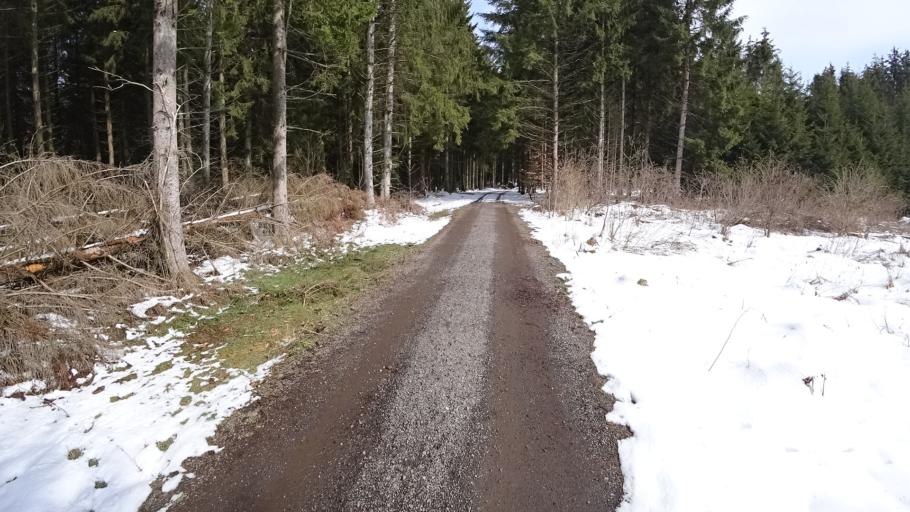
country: DE
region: Rheinland-Pfalz
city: Morlen
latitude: 50.7088
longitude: 7.8831
